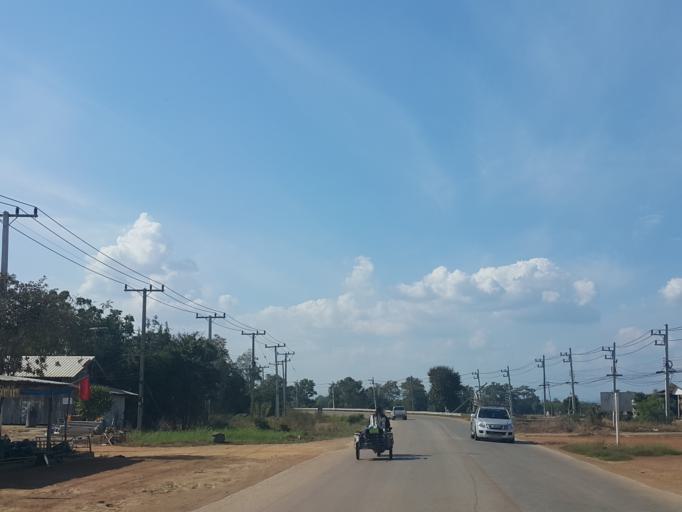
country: TH
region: Sukhothai
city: Sawankhalok
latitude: 17.3088
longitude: 99.7689
